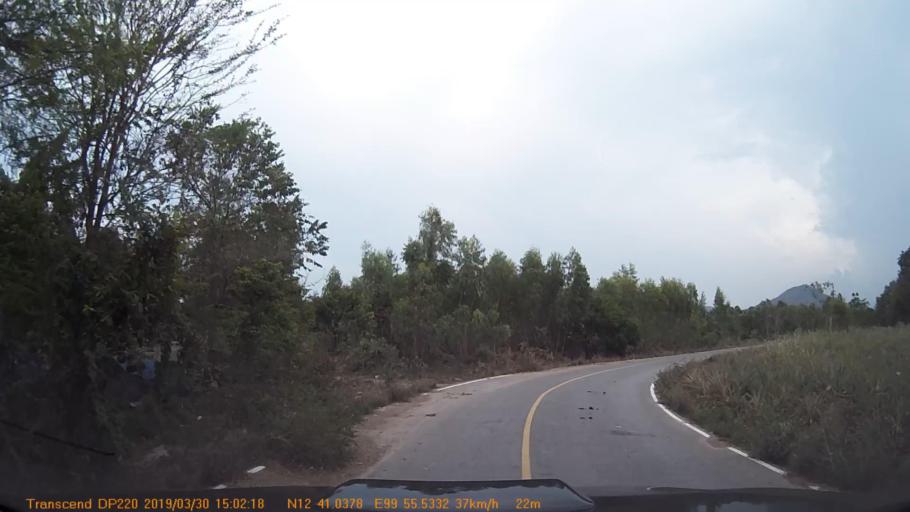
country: TH
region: Prachuap Khiri Khan
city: Hua Hin
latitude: 12.6837
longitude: 99.9253
